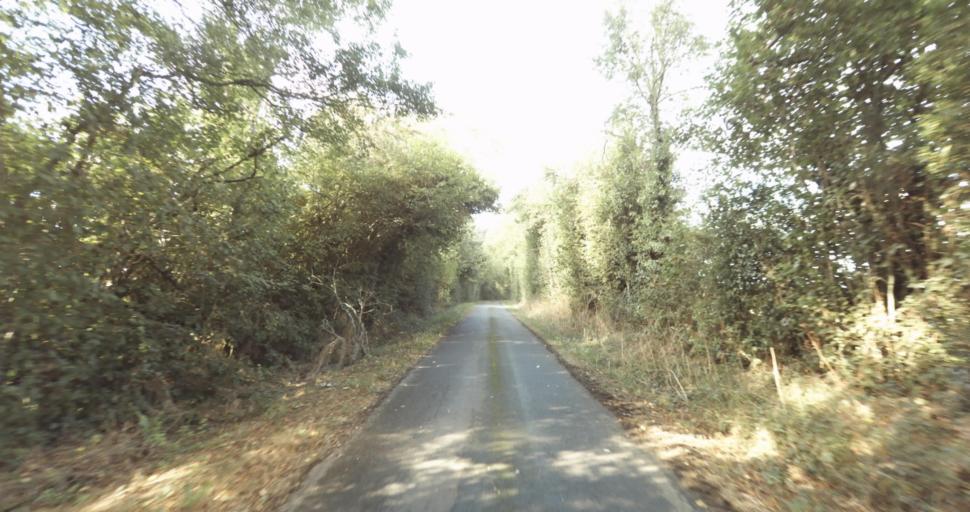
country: FR
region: Lower Normandy
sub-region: Departement de l'Orne
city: Vimoutiers
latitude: 48.9223
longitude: 0.1177
